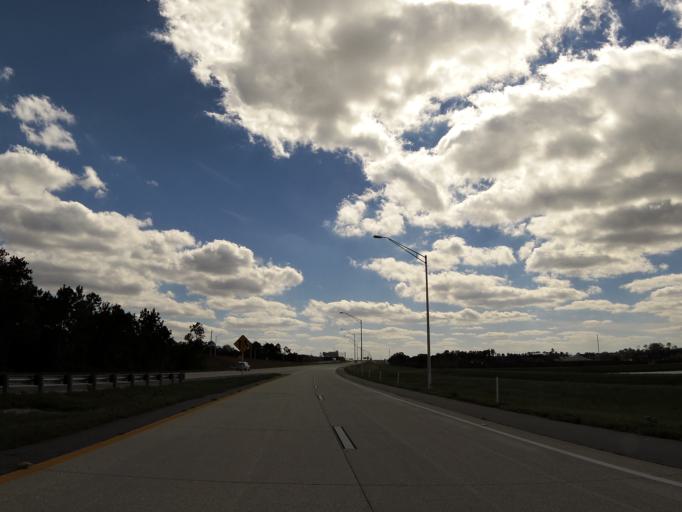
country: US
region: Florida
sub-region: Saint Johns County
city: Fruit Cove
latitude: 30.1113
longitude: -81.5152
